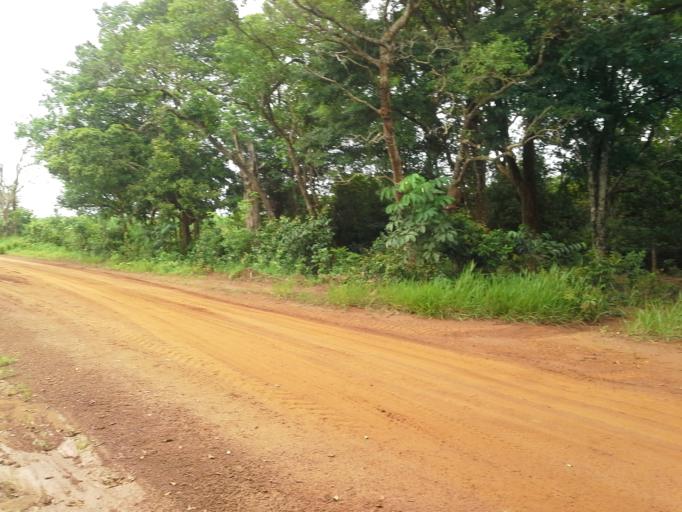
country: CO
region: Cundinamarca
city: Tibacuy
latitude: 4.1912
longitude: -72.4324
